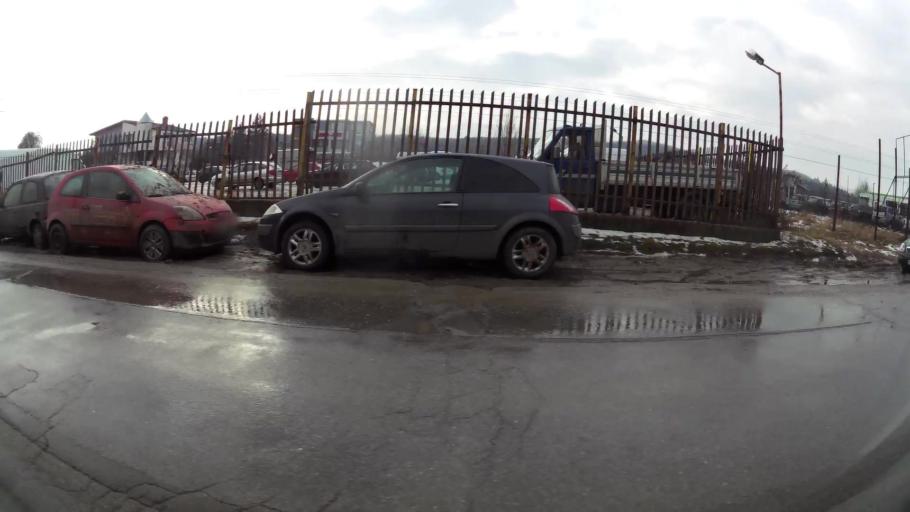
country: BG
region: Sofia-Capital
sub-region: Stolichna Obshtina
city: Sofia
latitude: 42.7097
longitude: 23.2623
